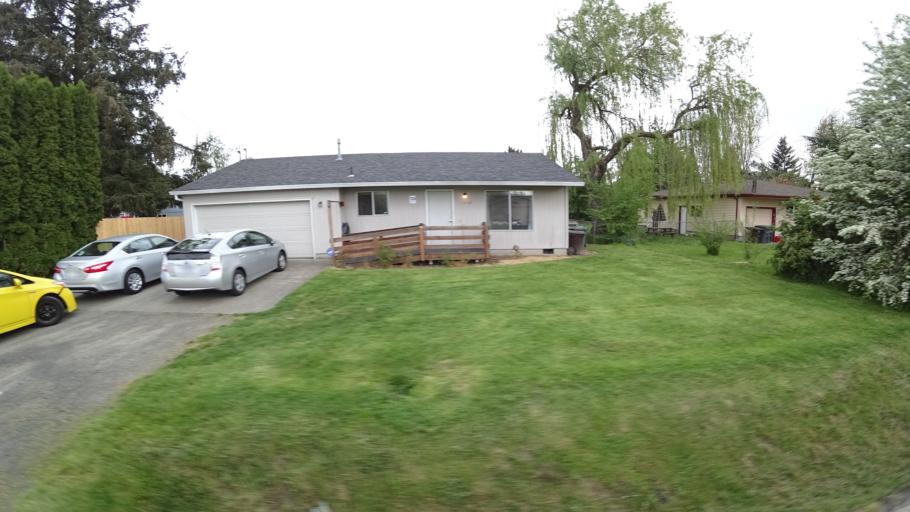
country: US
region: Oregon
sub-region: Washington County
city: Hillsboro
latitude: 45.5367
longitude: -122.9670
